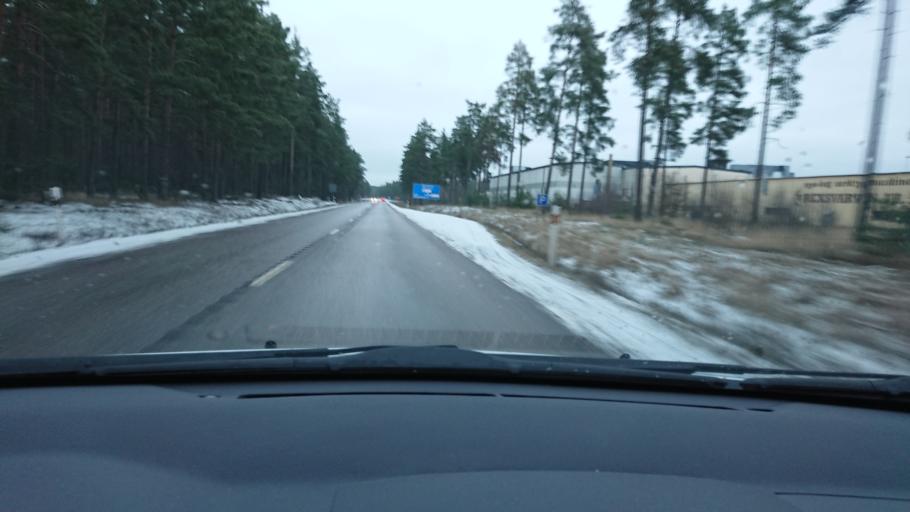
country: SE
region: Kalmar
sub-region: Hultsfreds Kommun
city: Hultsfred
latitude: 57.5074
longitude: 15.8312
